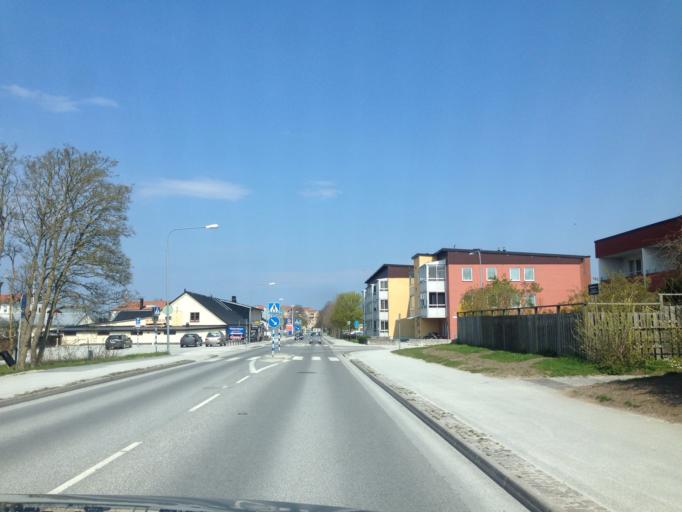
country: SE
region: Gotland
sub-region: Gotland
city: Visby
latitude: 57.6276
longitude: 18.2873
